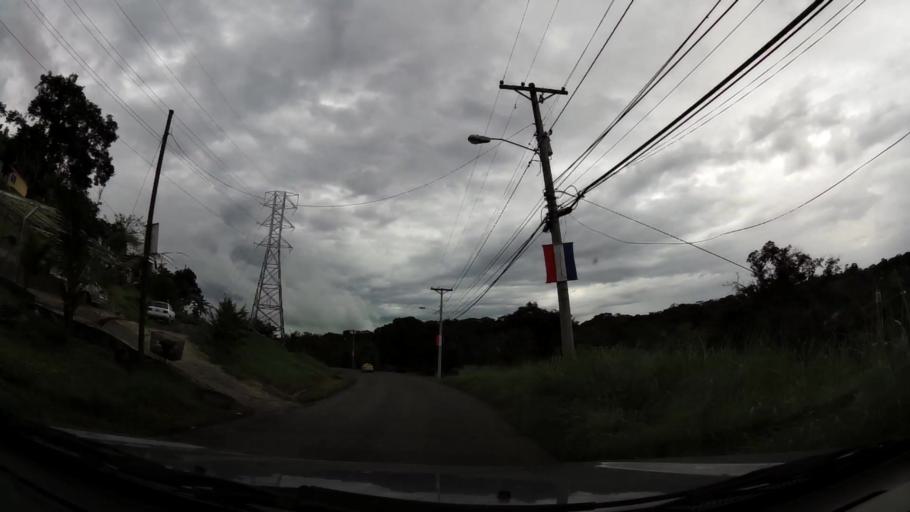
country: PA
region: Panama
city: Chilibre
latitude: 9.1673
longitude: -79.6133
